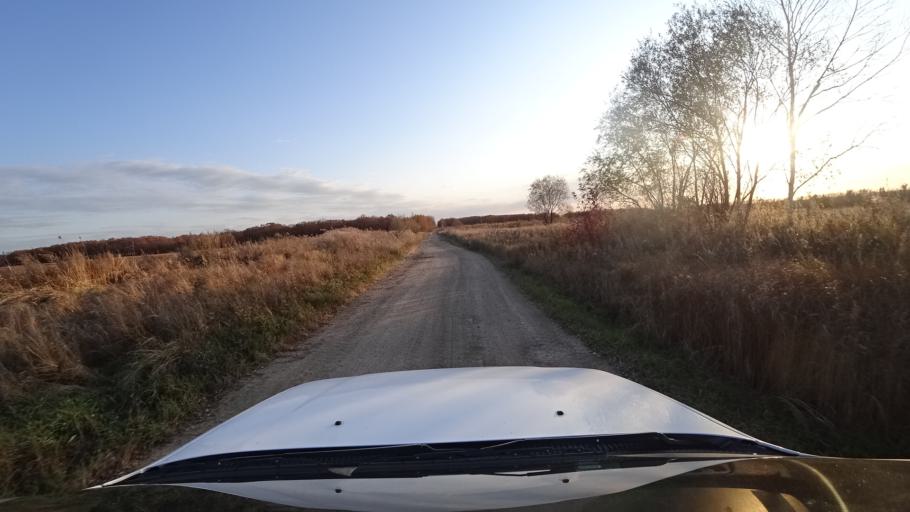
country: RU
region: Primorskiy
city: Lazo
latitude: 45.8093
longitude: 133.6072
